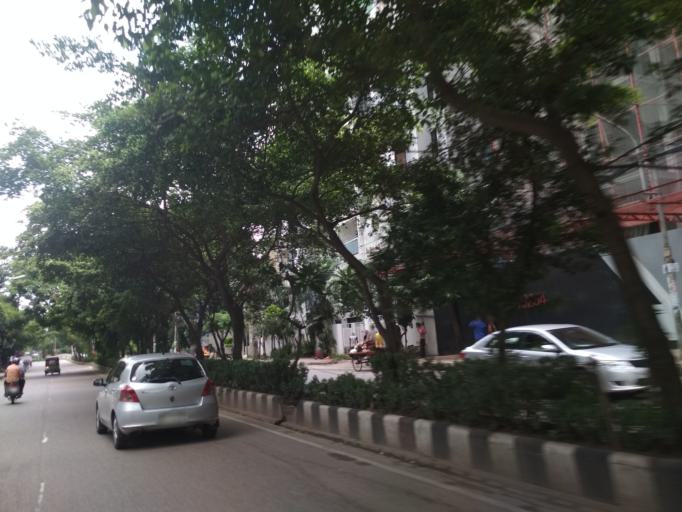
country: BD
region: Dhaka
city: Paltan
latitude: 23.7958
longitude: 90.4174
